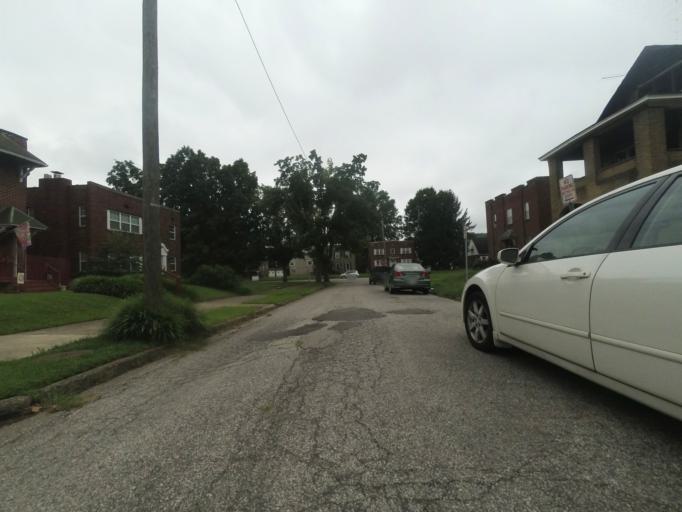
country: US
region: West Virginia
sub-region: Cabell County
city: Huntington
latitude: 38.4122
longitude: -82.4330
